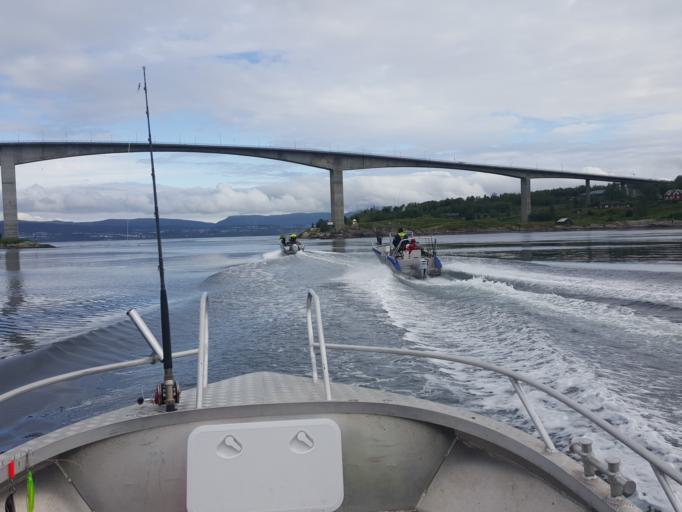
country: NO
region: Nordland
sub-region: Bodo
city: Loding
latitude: 67.2286
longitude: 14.6158
